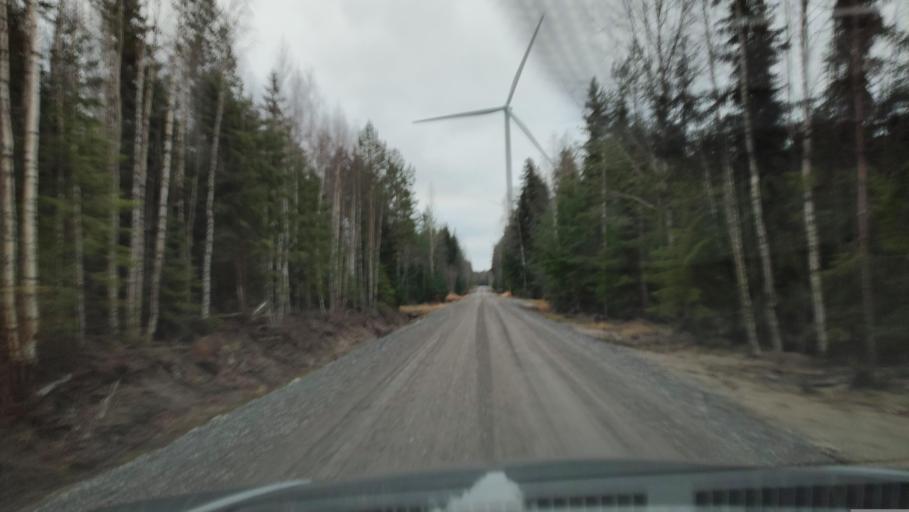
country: FI
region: Southern Ostrobothnia
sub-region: Suupohja
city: Karijoki
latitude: 62.2133
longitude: 21.6021
